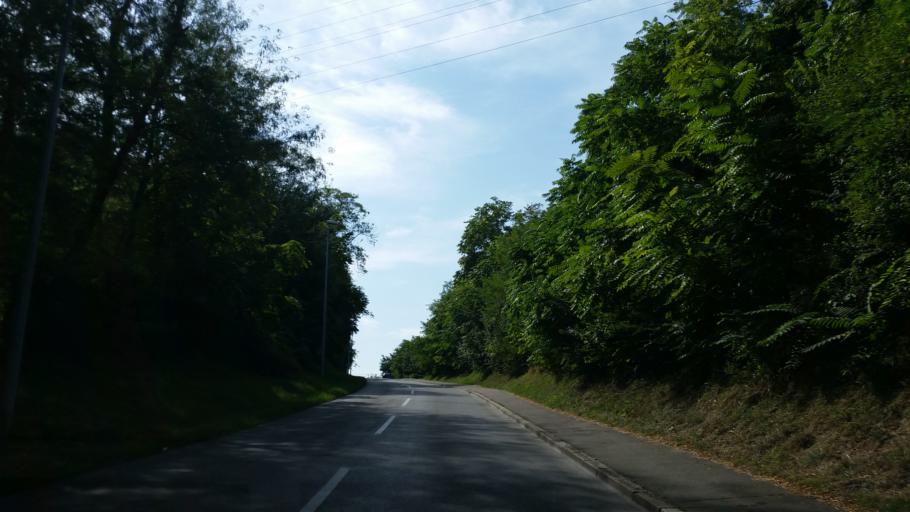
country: RS
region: Central Serbia
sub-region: Belgrade
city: Palilula
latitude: 44.8110
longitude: 20.5017
